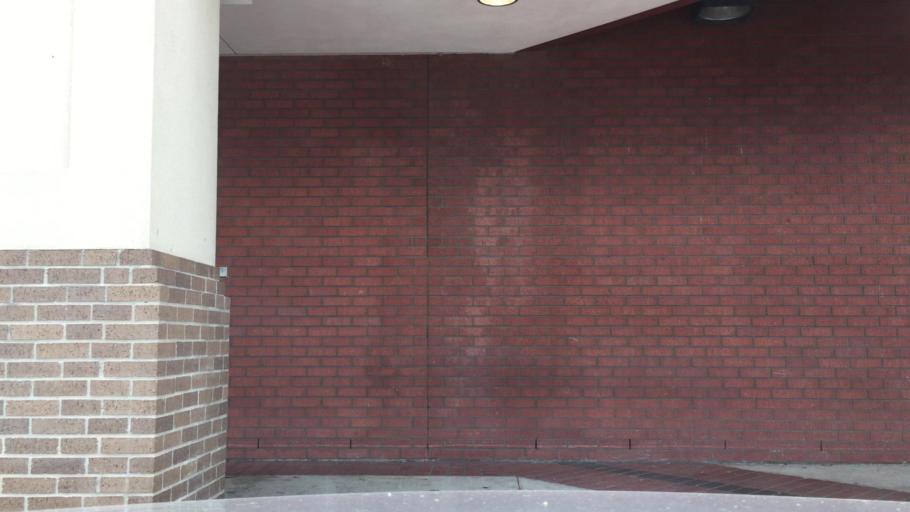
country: US
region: Texas
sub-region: Harris County
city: Hudson
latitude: 29.9661
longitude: -95.5426
